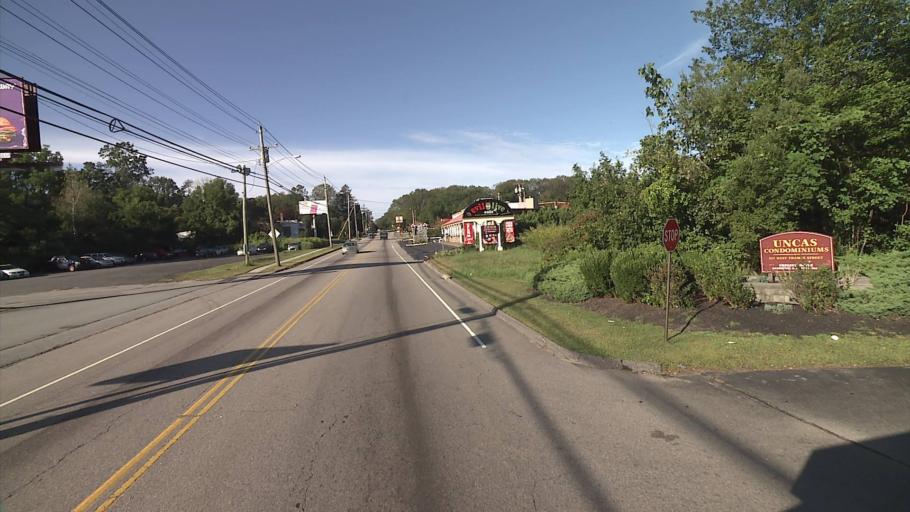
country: US
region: Connecticut
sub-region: New London County
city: Norwich
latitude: 41.5035
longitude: -72.0923
